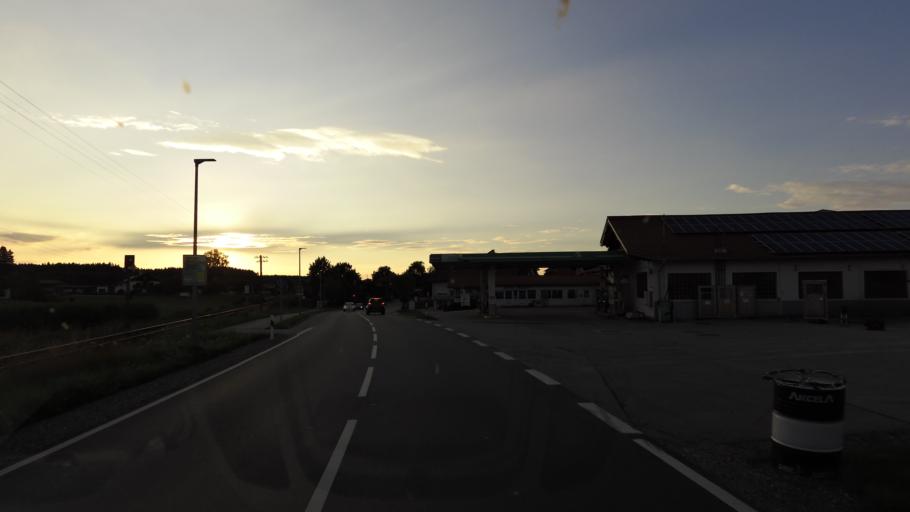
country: DE
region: Bavaria
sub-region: Upper Bavaria
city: Nussdorf
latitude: 47.9339
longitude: 12.5954
